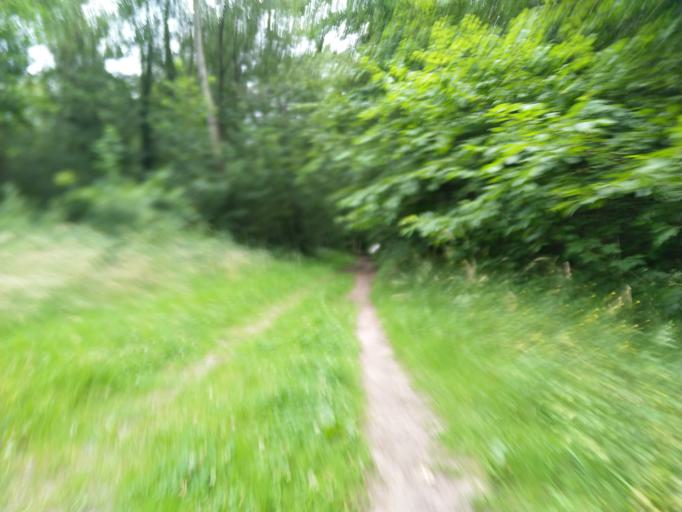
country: BE
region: Wallonia
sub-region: Province du Hainaut
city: Saint-Ghislain
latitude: 50.4888
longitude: 3.8447
